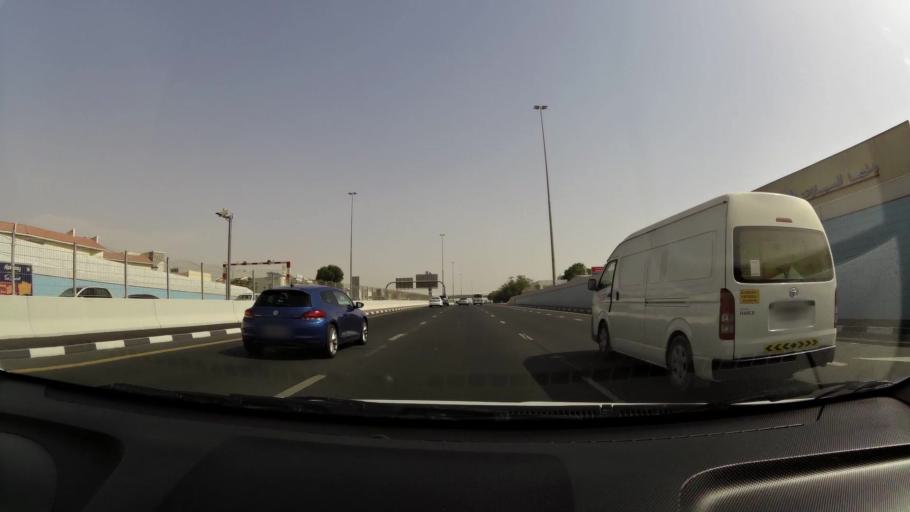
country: AE
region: Ash Shariqah
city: Sharjah
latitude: 25.2348
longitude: 55.3777
